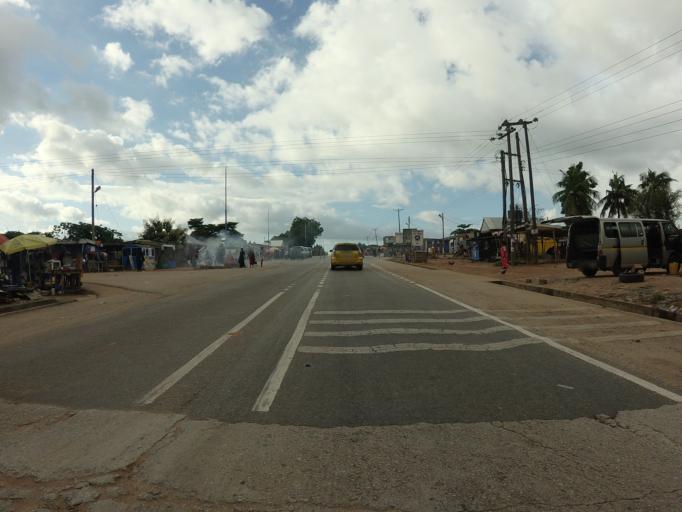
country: GH
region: Ashanti
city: Tafo
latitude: 6.8359
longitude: -1.6506
